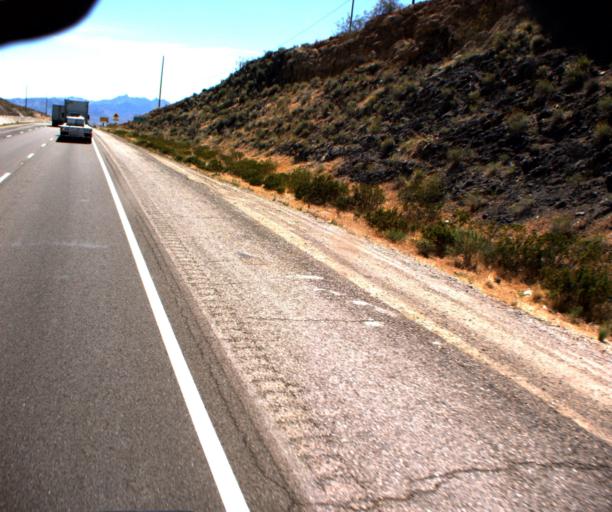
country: US
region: Arizona
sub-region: Mohave County
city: Kingman
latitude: 35.2089
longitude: -114.1034
